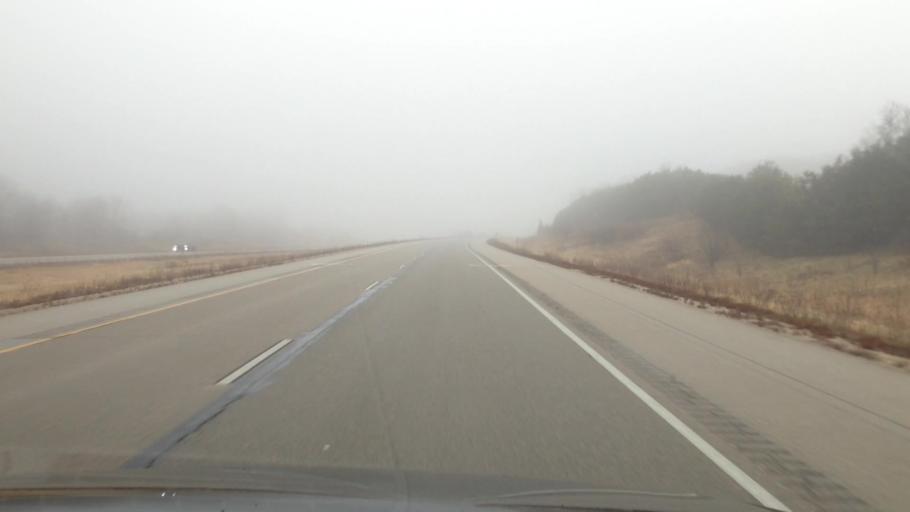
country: US
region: Wisconsin
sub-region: Walworth County
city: Elkhorn
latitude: 42.7111
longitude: -88.4793
